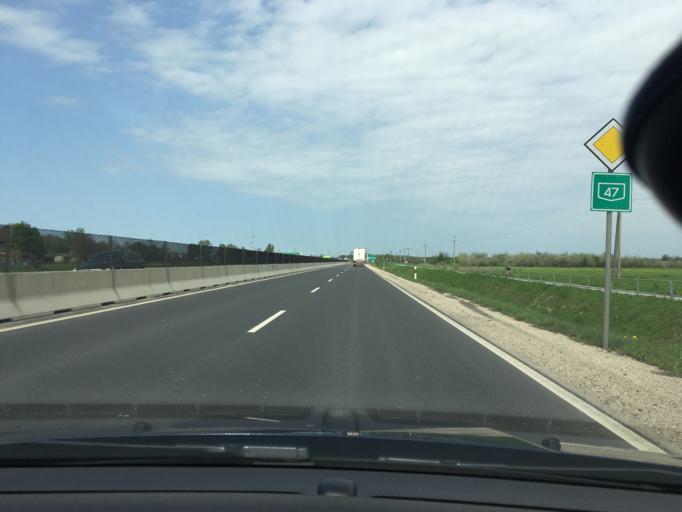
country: HU
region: Csongrad
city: Algyo
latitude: 46.3120
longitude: 20.1866
